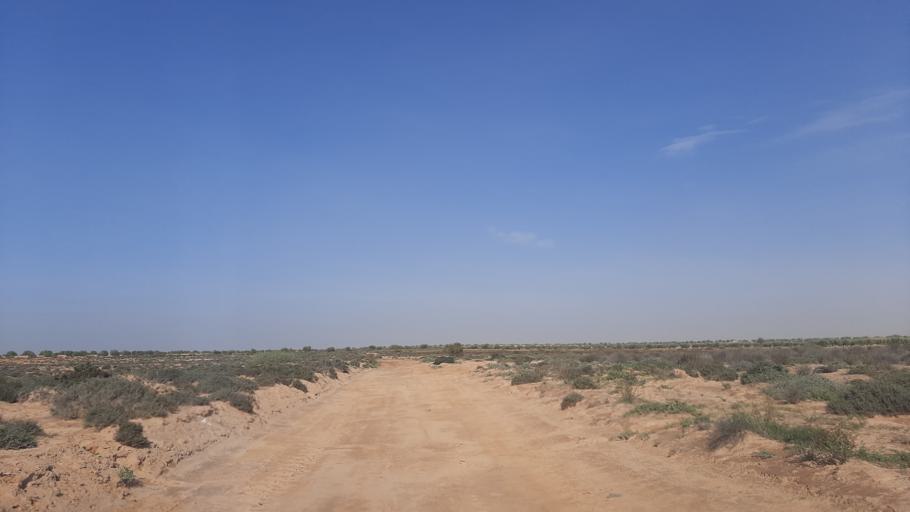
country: TN
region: Madanin
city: Zarzis
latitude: 33.4497
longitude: 10.8080
